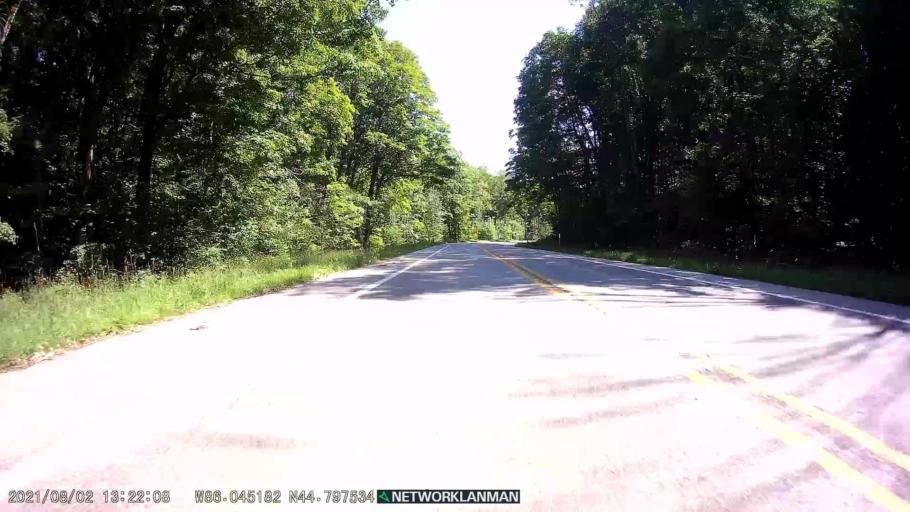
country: US
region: Michigan
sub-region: Benzie County
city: Beulah
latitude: 44.7984
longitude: -86.0452
